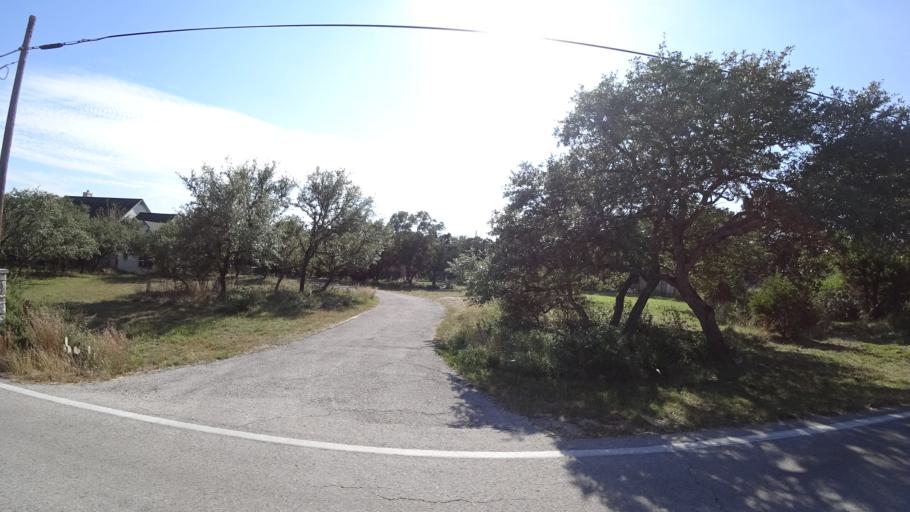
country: US
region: Texas
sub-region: Travis County
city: Barton Creek
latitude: 30.2279
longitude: -97.9088
